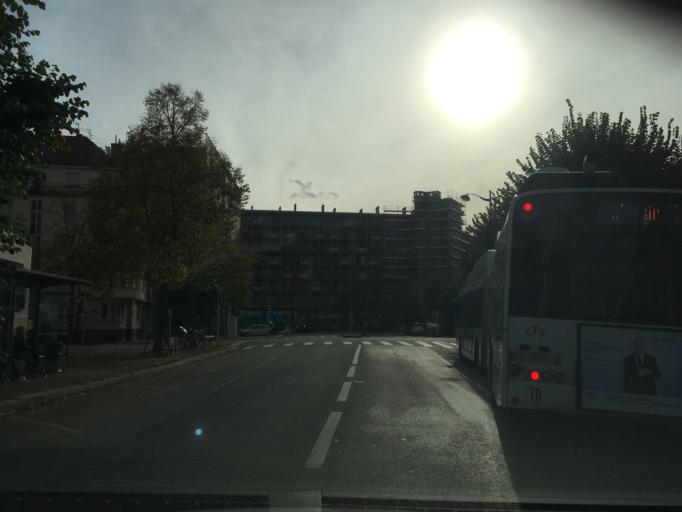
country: FR
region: Alsace
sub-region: Departement du Bas-Rhin
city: Strasbourg
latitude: 48.5863
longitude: 7.7808
